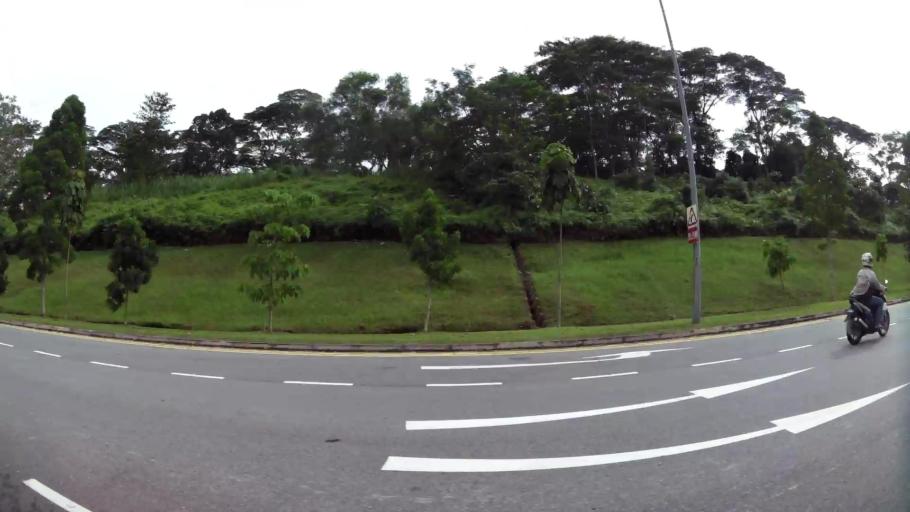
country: MY
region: Johor
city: Johor Bahru
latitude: 1.4163
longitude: 103.7649
